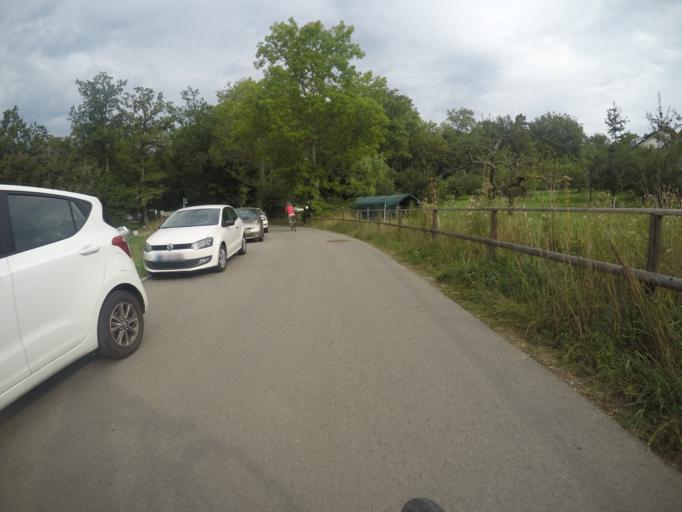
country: DE
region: Baden-Wuerttemberg
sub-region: Regierungsbezirk Stuttgart
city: Stuttgart
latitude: 48.7453
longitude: 9.1457
